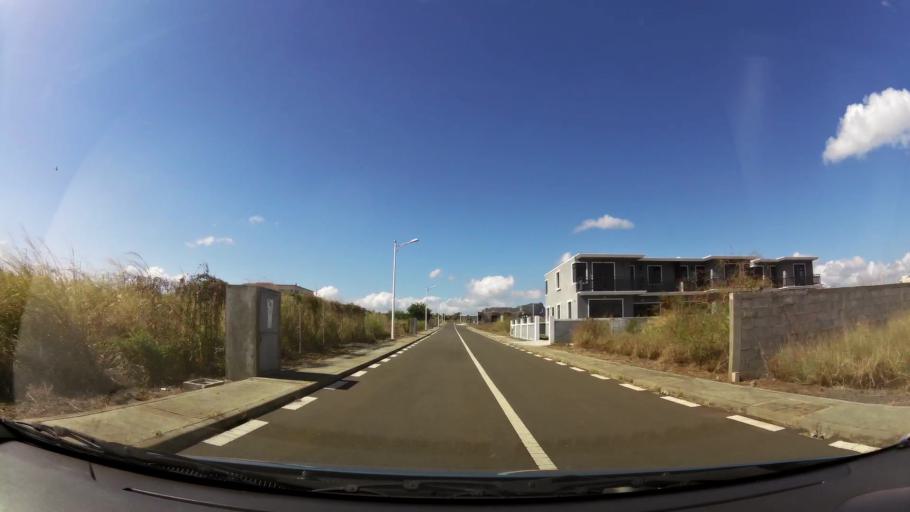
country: MU
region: Black River
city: Flic en Flac
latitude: -20.2784
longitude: 57.3835
